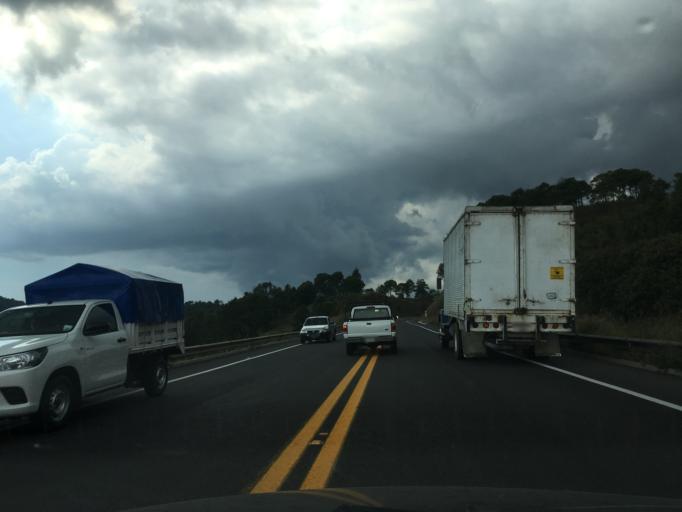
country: MX
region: Michoacan
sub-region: Uruapan
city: Toreo Bajo (El Toreo Bajo)
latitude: 19.4150
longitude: -101.9775
